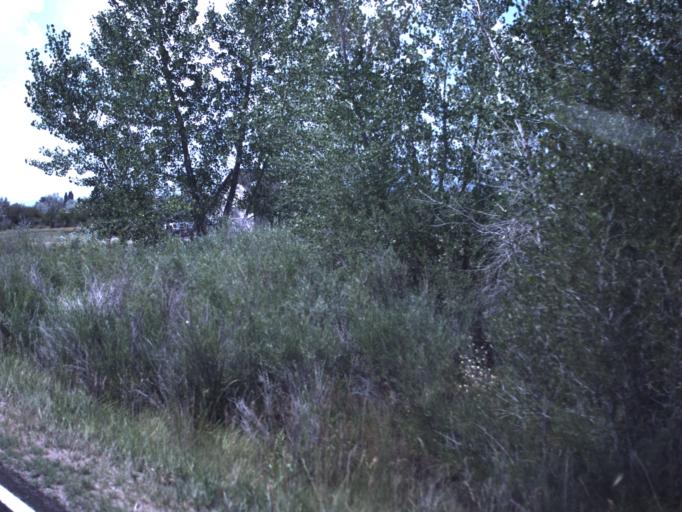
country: US
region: Utah
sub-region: Duchesne County
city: Roosevelt
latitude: 40.4038
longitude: -109.9080
